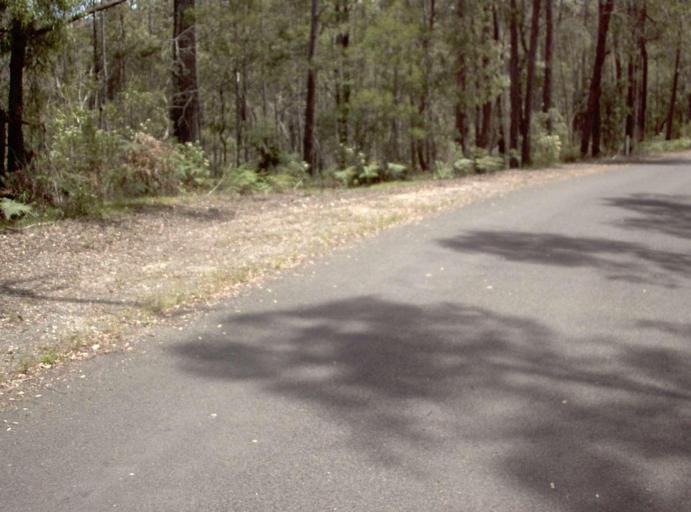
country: AU
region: New South Wales
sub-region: Bombala
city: Bombala
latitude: -37.4436
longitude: 148.9789
